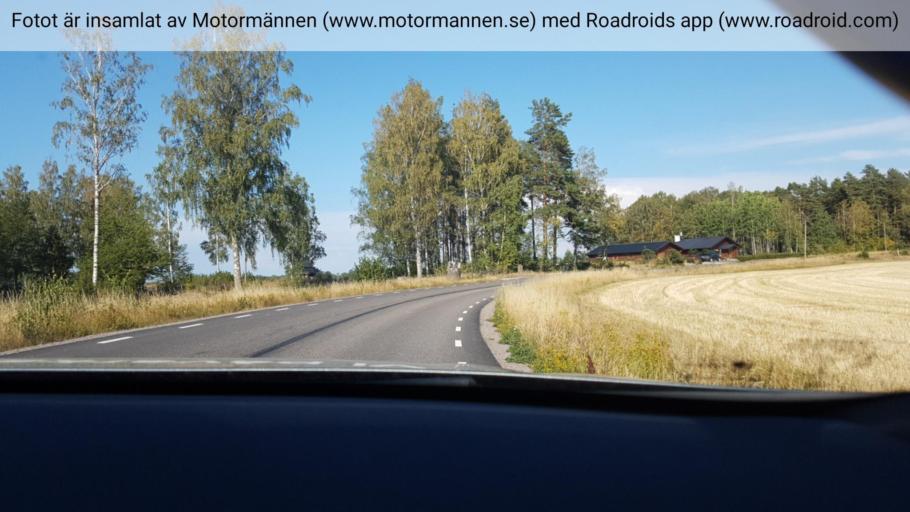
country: SE
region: Vaestra Goetaland
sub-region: Mariestads Kommun
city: Mariestad
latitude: 58.6410
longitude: 13.6780
